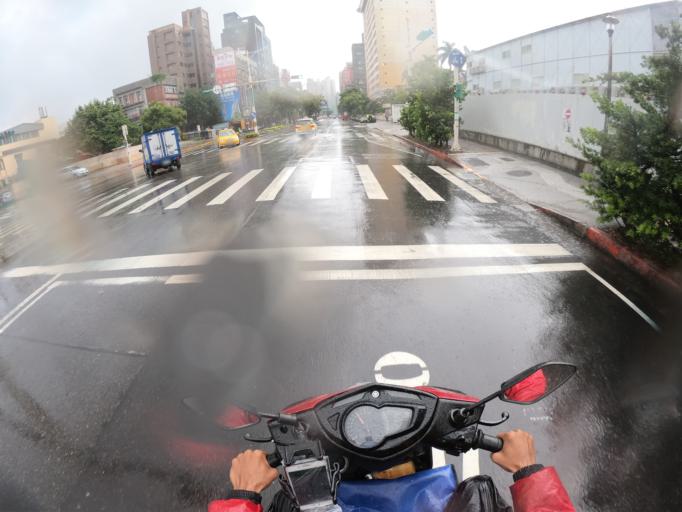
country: TW
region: Taipei
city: Taipei
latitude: 25.0408
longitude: 121.5694
